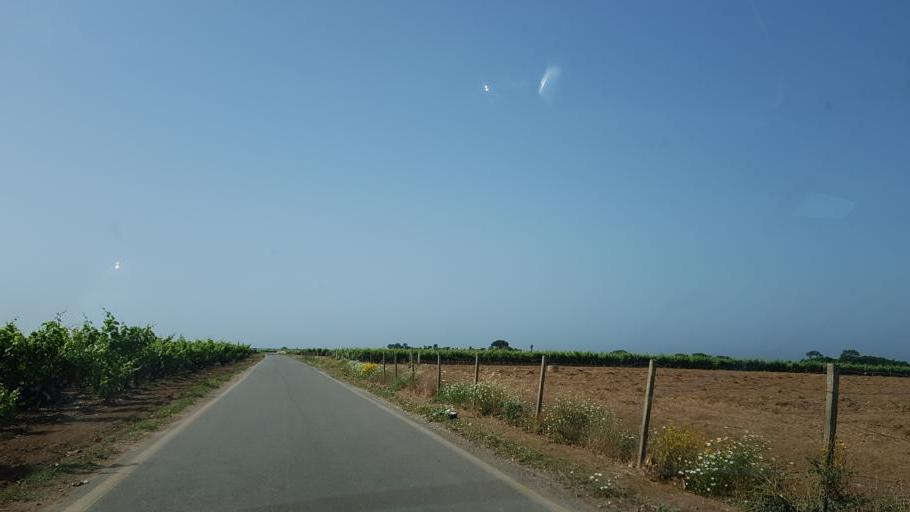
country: IT
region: Apulia
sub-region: Provincia di Brindisi
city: Brindisi
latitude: 40.6719
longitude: 17.8876
